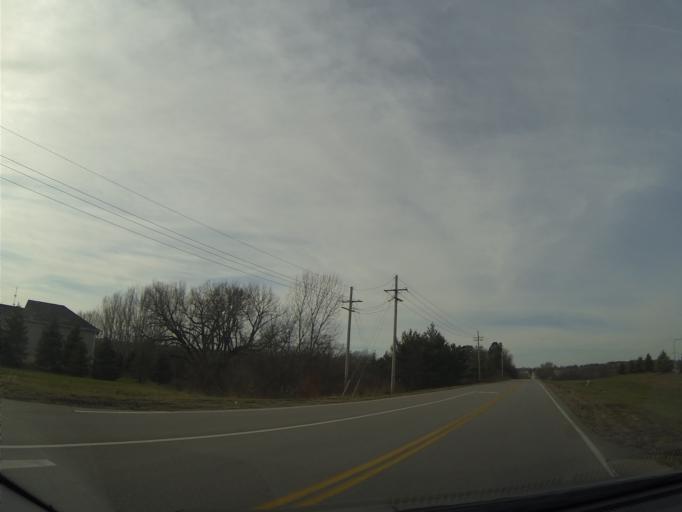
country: US
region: Nebraska
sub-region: Douglas County
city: Elkhorn
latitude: 41.2776
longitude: -96.1919
